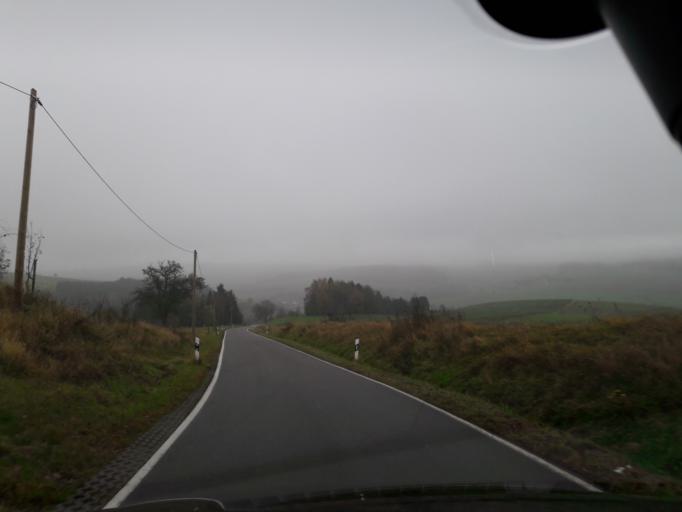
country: DE
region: Rheinland-Pfalz
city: Wahnwegen
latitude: 49.4715
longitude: 7.3927
